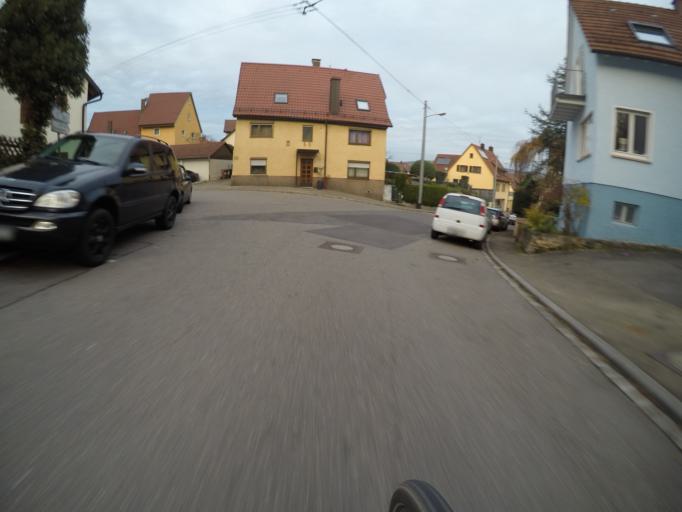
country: DE
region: Baden-Wuerttemberg
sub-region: Regierungsbezirk Stuttgart
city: Ostfildern
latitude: 48.7554
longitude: 9.2545
